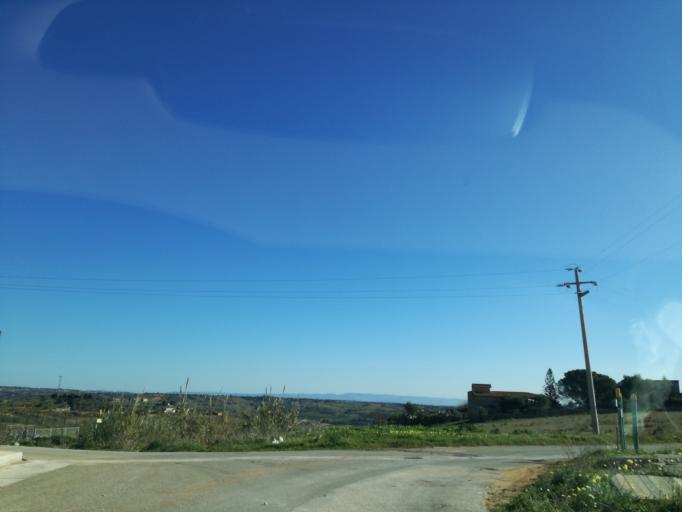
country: IT
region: Sicily
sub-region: Provincia di Caltanissetta
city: Niscemi
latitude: 37.0595
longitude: 14.3572
